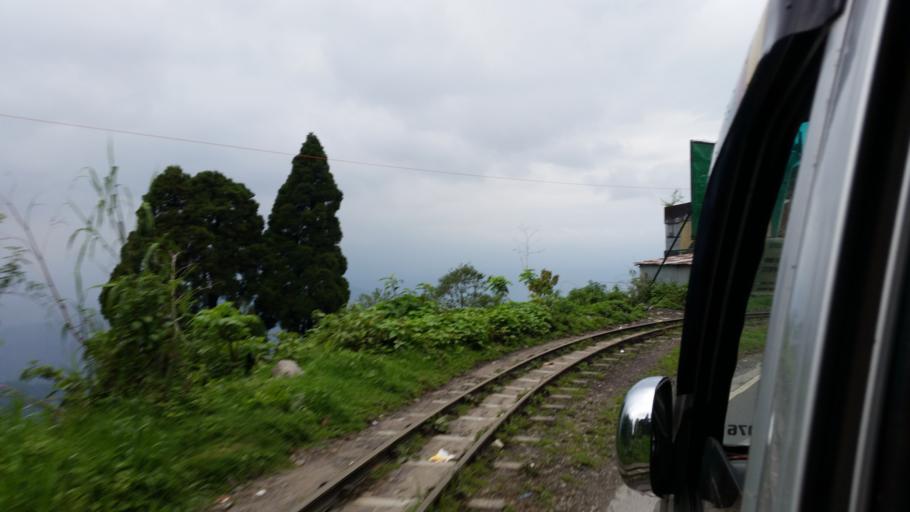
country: IN
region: West Bengal
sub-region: Darjiling
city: Darjiling
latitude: 27.0200
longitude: 88.2502
